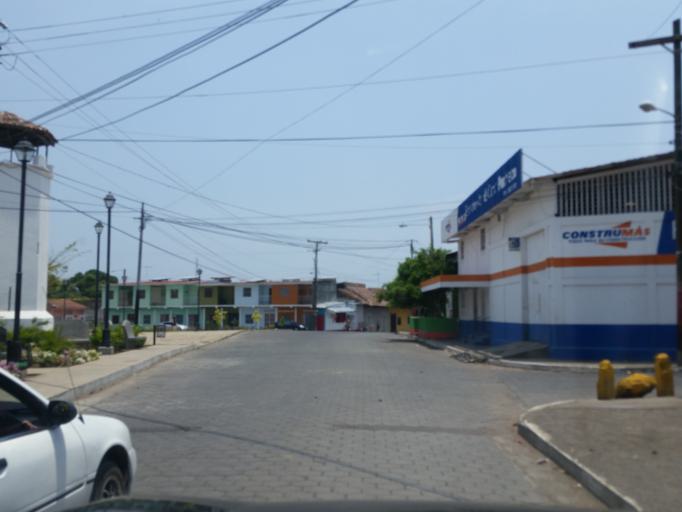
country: NI
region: Granada
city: Granada
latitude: 11.9282
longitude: -85.9653
